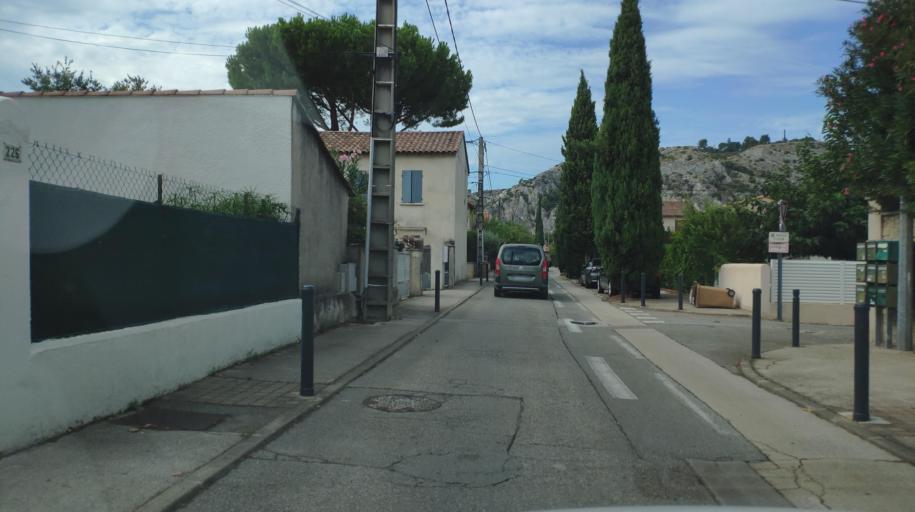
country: FR
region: Provence-Alpes-Cote d'Azur
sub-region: Departement du Vaucluse
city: Cavaillon
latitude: 43.8298
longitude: 5.0341
